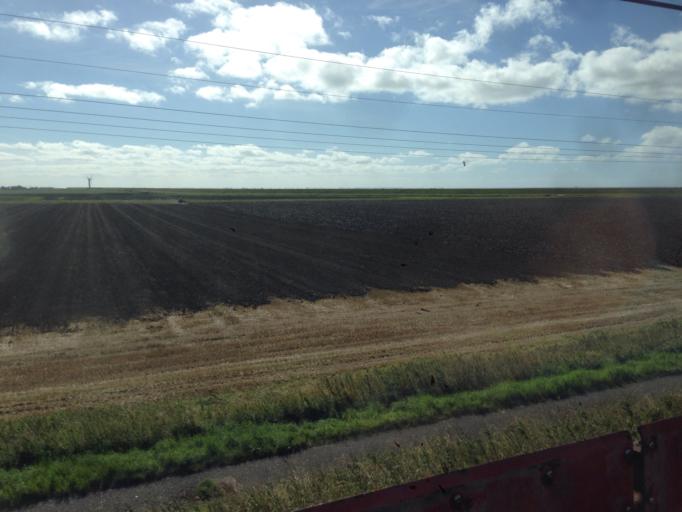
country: DE
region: Schleswig-Holstein
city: Friedrich-Wilhelm-Lubke-Koog
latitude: 54.8868
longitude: 8.6180
